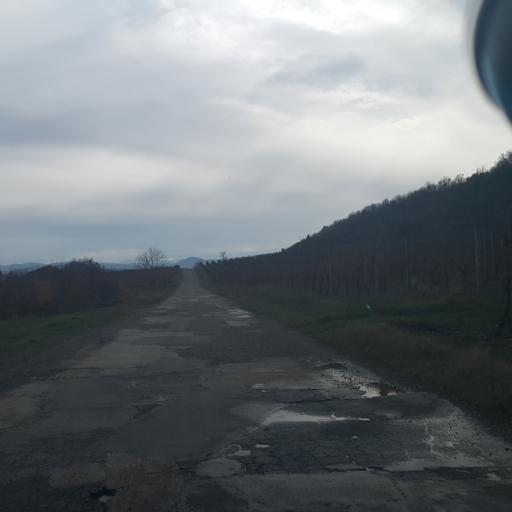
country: RS
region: Central Serbia
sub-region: Zajecarski Okrug
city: Knjazevac
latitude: 43.6184
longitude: 22.2611
